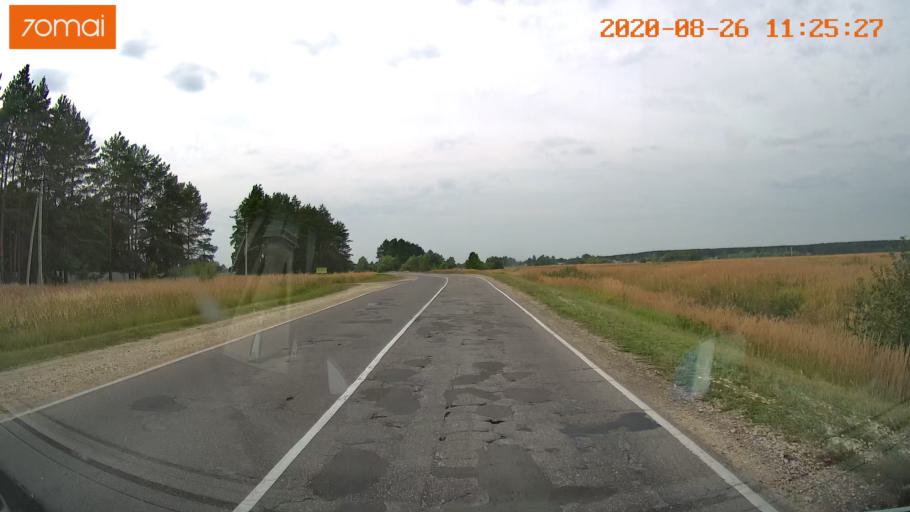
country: RU
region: Rjazan
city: Shilovo
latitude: 54.3418
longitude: 40.9644
